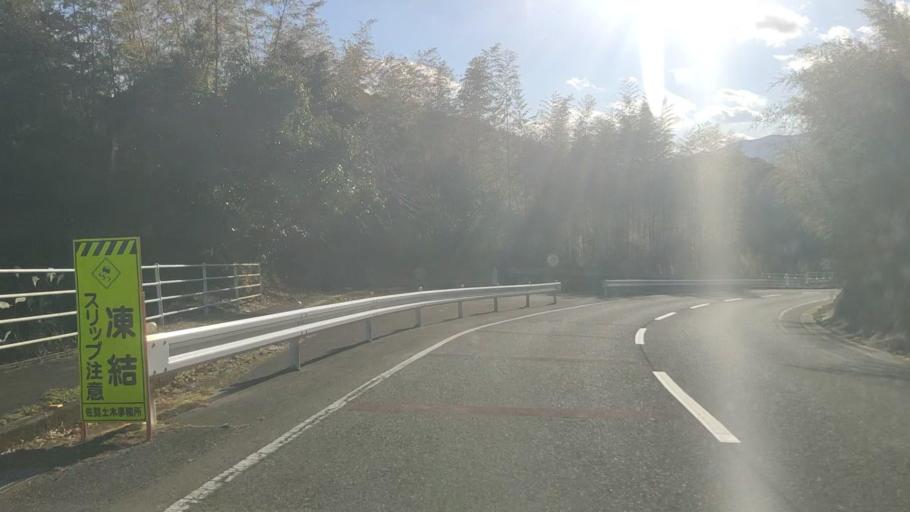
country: JP
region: Saga Prefecture
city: Kanzakimachi-kanzaki
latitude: 33.3899
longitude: 130.2659
